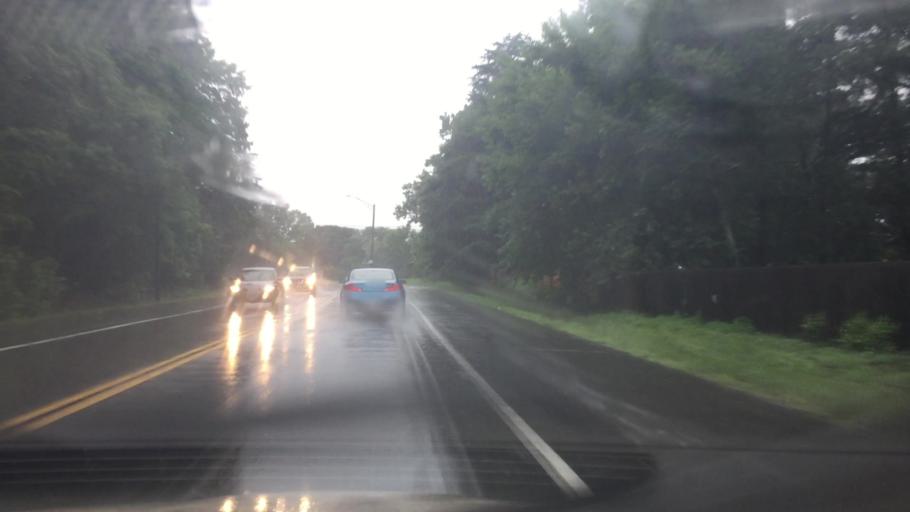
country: US
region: Maryland
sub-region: Anne Arundel County
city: Severn
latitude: 39.1352
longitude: -76.7013
